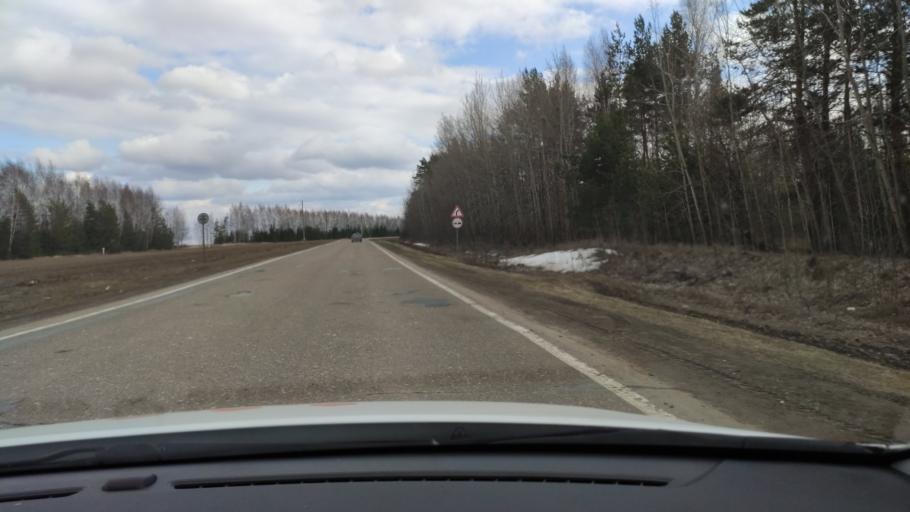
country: RU
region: Tatarstan
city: Vysokaya Gora
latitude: 56.0638
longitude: 49.2026
